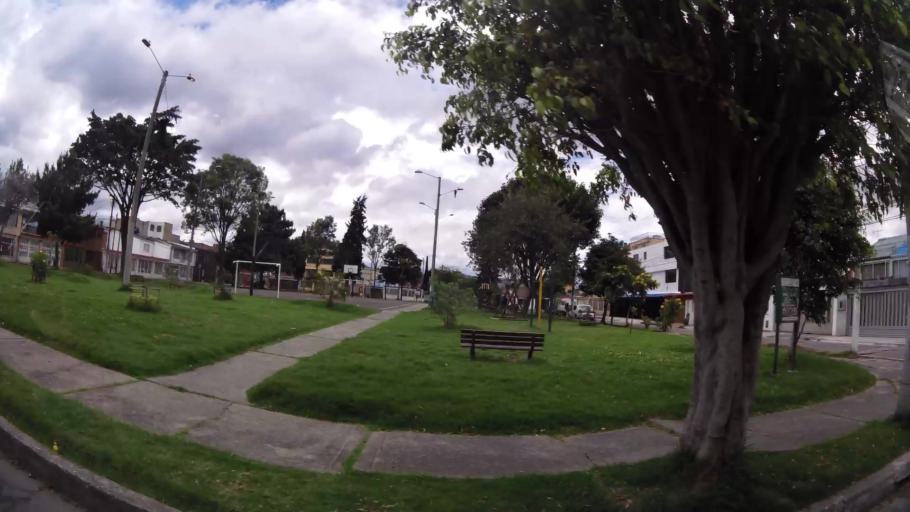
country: CO
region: Bogota D.C.
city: Bogota
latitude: 4.6059
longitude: -74.1133
